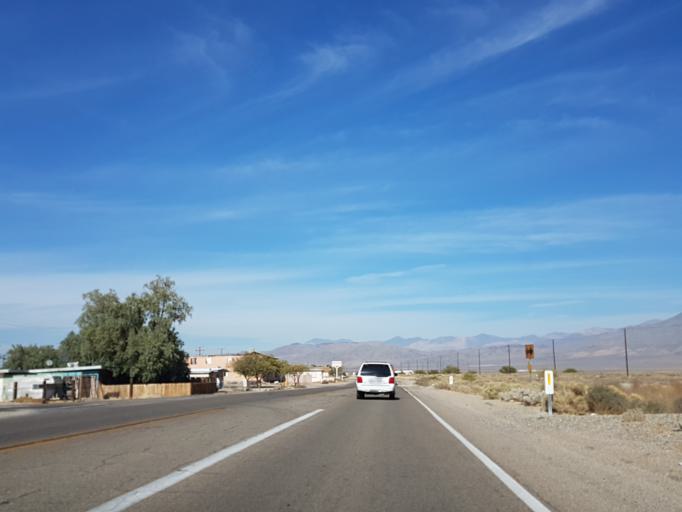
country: US
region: California
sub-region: San Bernardino County
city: Searles Valley
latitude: 35.7843
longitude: -117.3635
